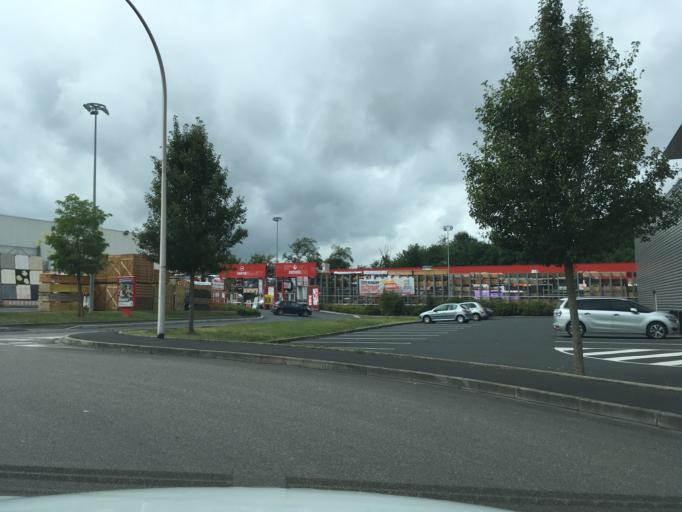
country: FR
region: Limousin
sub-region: Departement de la Correze
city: Saint-Pantaleon-de-Larche
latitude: 45.1460
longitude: 1.4701
